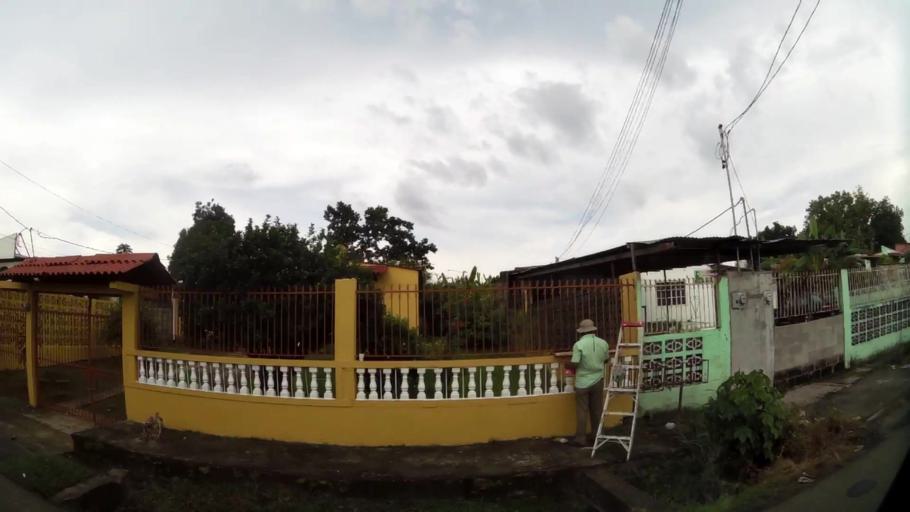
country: PA
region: Panama
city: Tocumen
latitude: 9.1043
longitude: -79.3660
